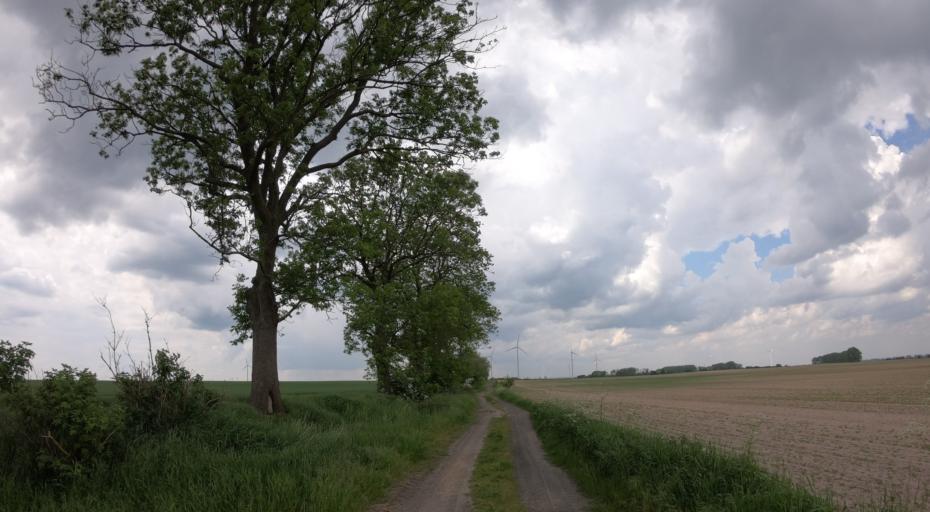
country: PL
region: West Pomeranian Voivodeship
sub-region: Powiat pyrzycki
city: Kozielice
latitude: 53.1047
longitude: 14.8684
